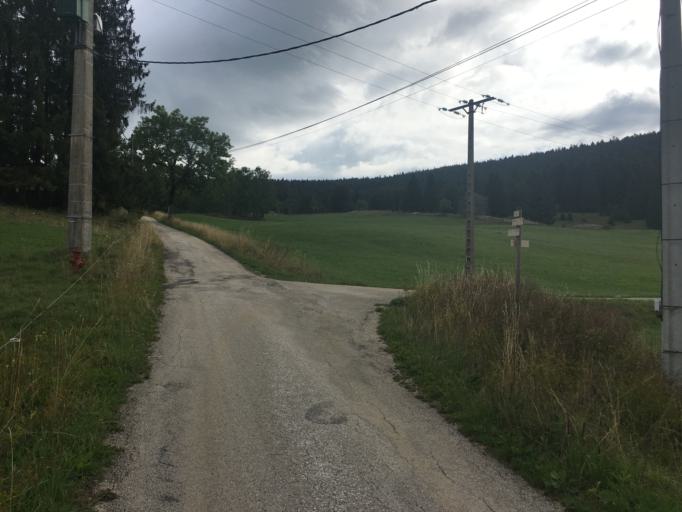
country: FR
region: Franche-Comte
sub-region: Departement du Jura
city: Morbier
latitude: 46.5553
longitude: 6.0310
